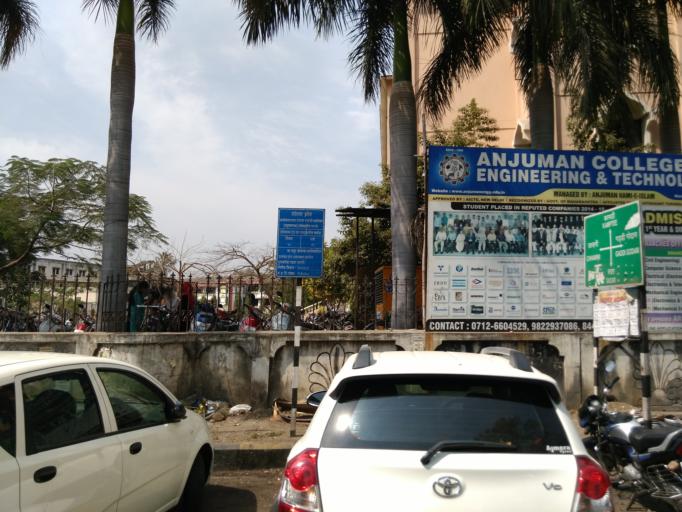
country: IN
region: Maharashtra
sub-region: Nagpur Division
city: Nagpur
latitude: 21.1645
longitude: 79.0811
